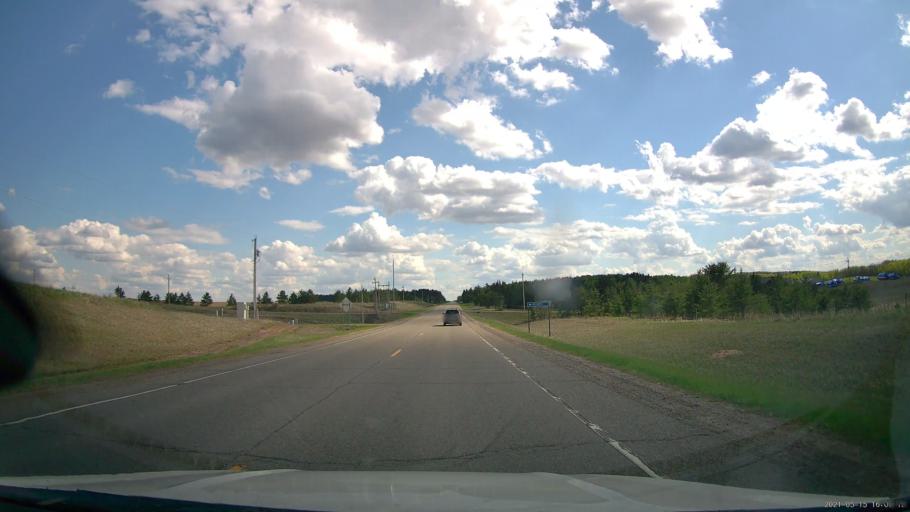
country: US
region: Minnesota
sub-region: Hubbard County
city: Park Rapids
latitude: 46.9519
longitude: -94.9528
